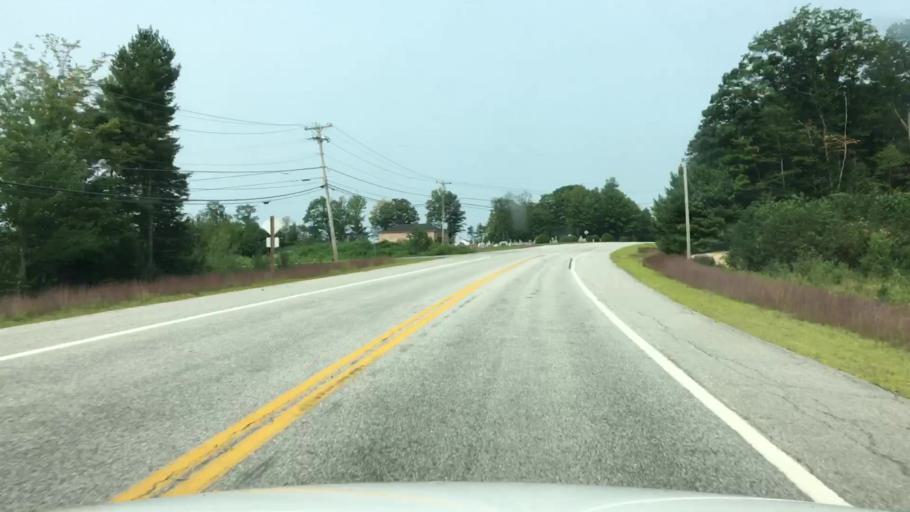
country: US
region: Maine
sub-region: Androscoggin County
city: Livermore Falls
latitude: 44.4480
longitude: -70.1602
